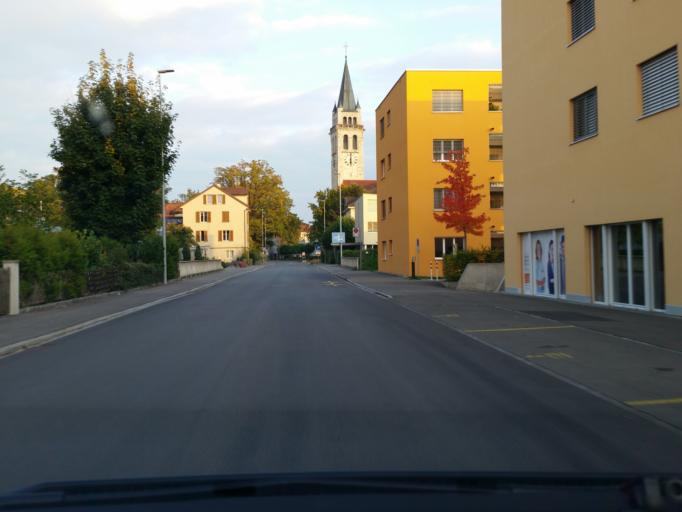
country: CH
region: Thurgau
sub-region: Arbon District
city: Romanshorn
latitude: 47.5696
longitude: 9.3781
